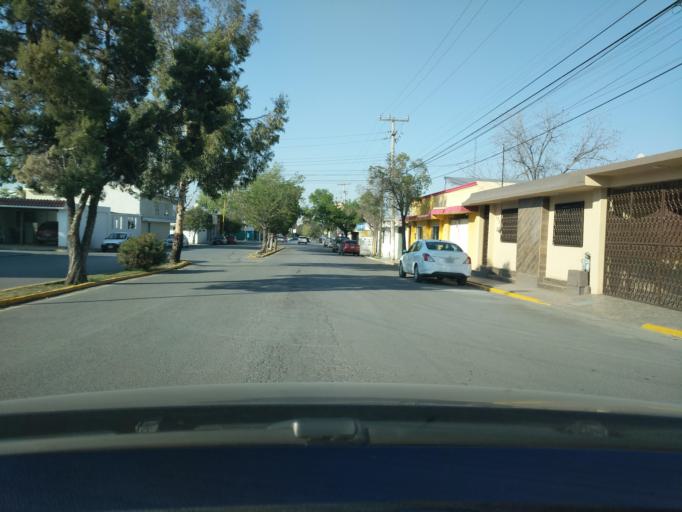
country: MX
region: Coahuila
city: Saltillo
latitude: 25.4663
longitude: -100.9858
